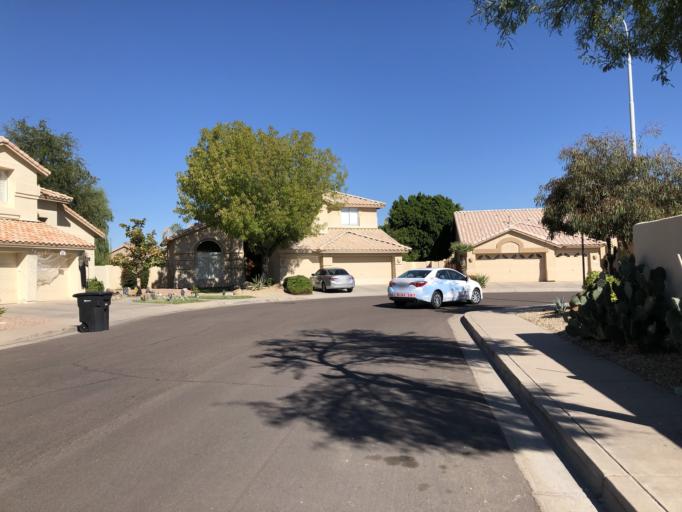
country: US
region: Arizona
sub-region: Maricopa County
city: Guadalupe
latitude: 33.3086
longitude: -111.9232
